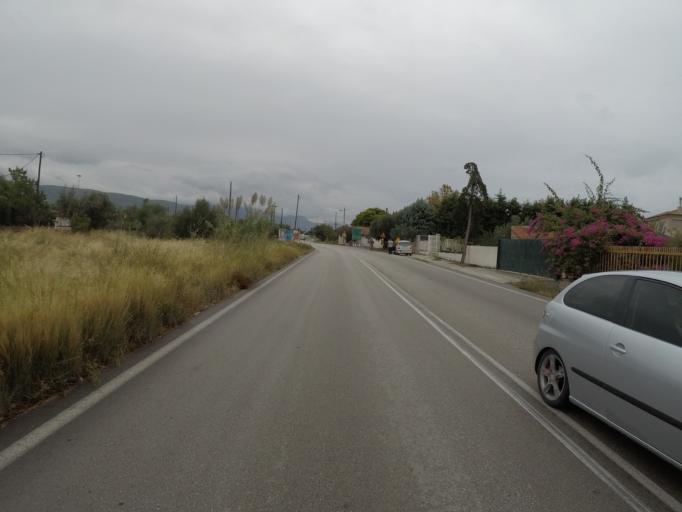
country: GR
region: Peloponnese
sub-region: Nomos Korinthias
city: Agioi Theodoroi
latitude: 37.9194
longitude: 23.1192
